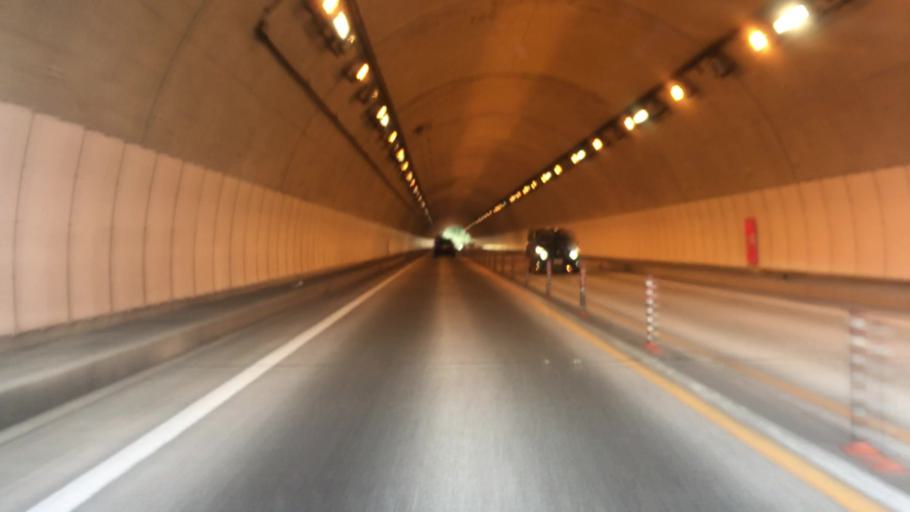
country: JP
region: Kyoto
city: Fukuchiyama
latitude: 35.2647
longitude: 135.0057
